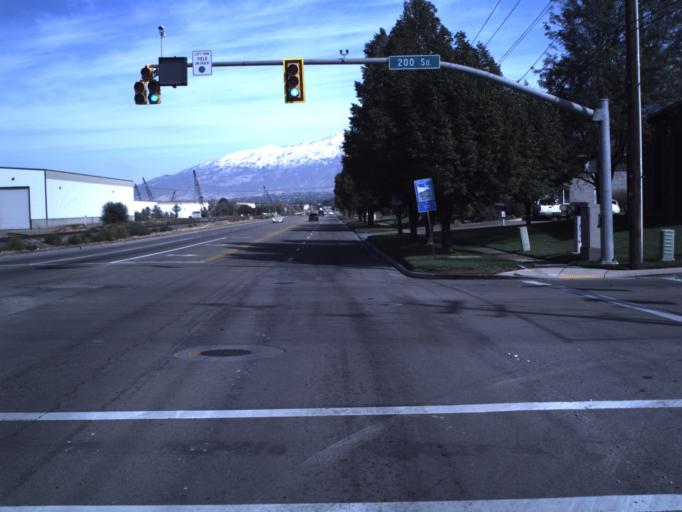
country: US
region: Utah
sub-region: Utah County
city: Lindon
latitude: 40.3334
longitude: -111.7386
